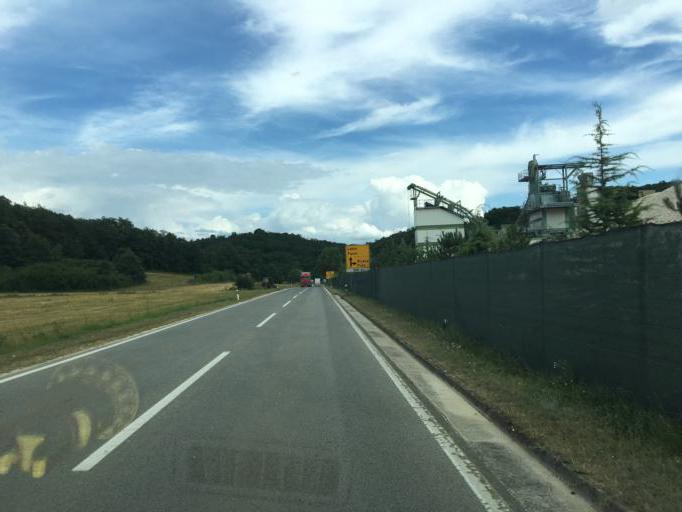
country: HR
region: Istarska
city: Pazin
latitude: 45.2422
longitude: 13.9073
